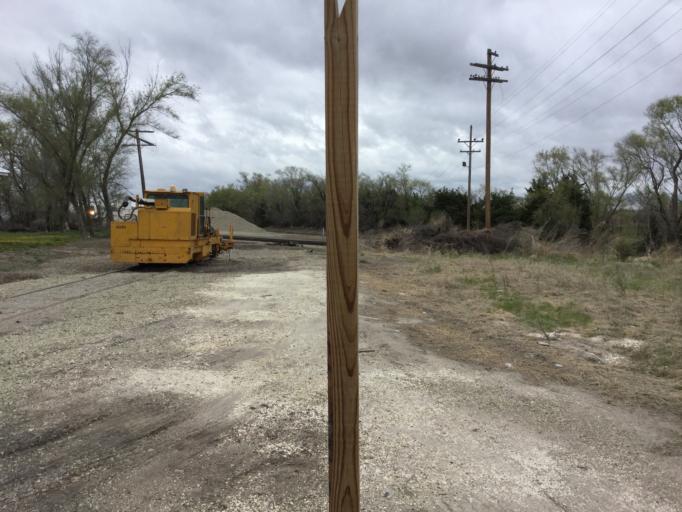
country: US
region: Kansas
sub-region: Phillips County
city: Phillipsburg
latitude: 39.7625
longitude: -99.3232
